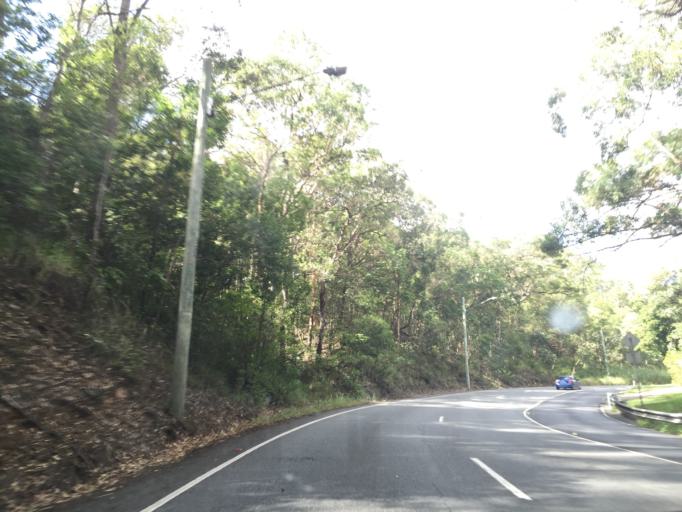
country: AU
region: Queensland
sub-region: Moreton Bay
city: Ferny Hills
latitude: -27.4273
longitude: 152.9445
